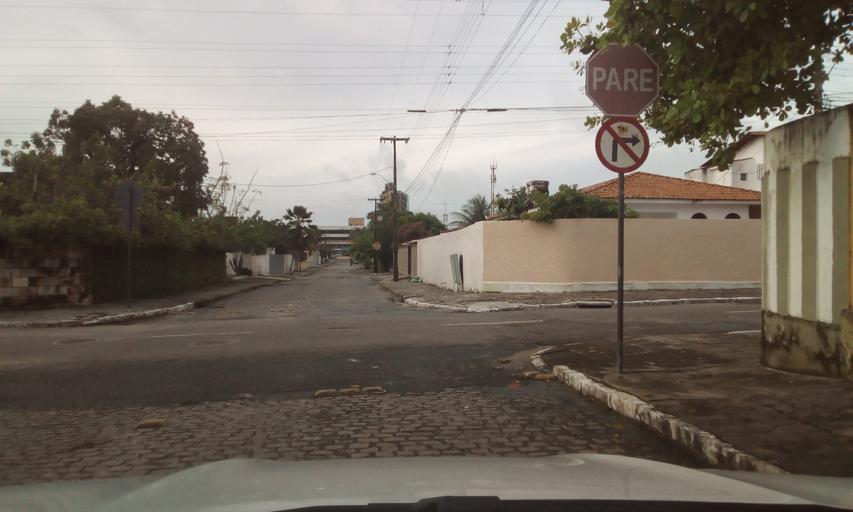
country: BR
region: Paraiba
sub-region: Joao Pessoa
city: Joao Pessoa
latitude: -7.1137
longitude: -34.8572
